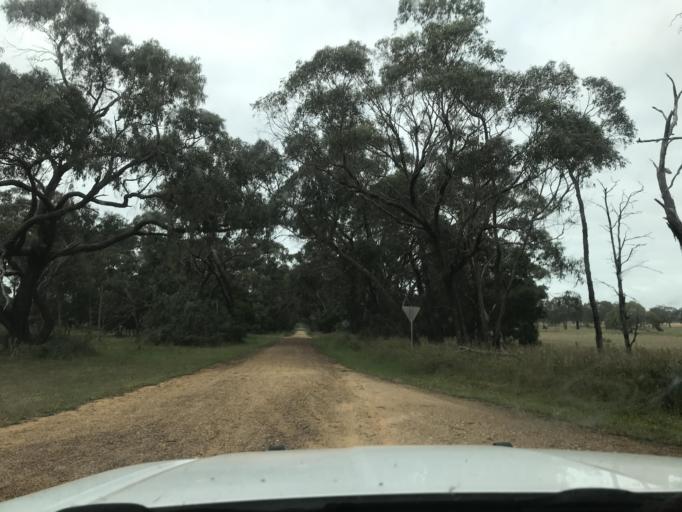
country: AU
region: South Australia
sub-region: Naracoorte and Lucindale
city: Naracoorte
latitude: -37.0857
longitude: 141.1217
